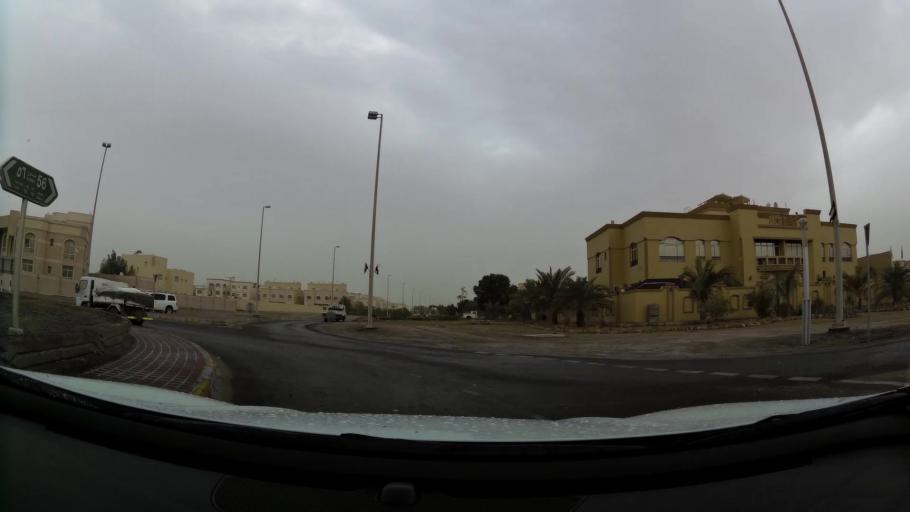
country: AE
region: Abu Dhabi
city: Abu Dhabi
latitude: 24.4134
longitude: 54.5861
